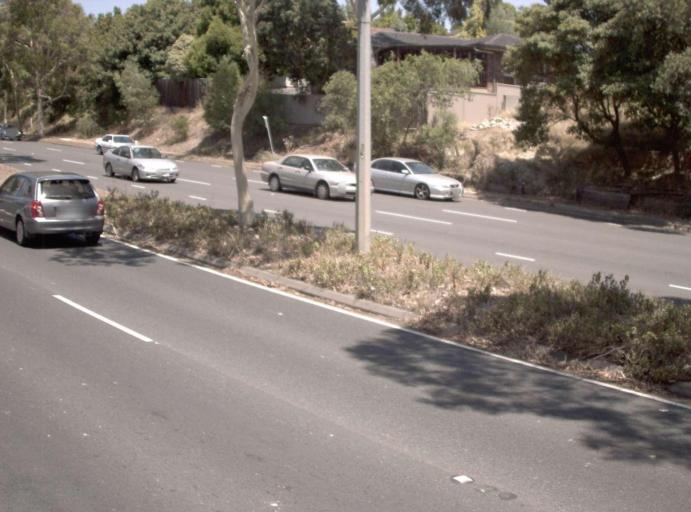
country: AU
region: Victoria
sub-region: Whitehorse
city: Vermont South
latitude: -37.8624
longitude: 145.1692
